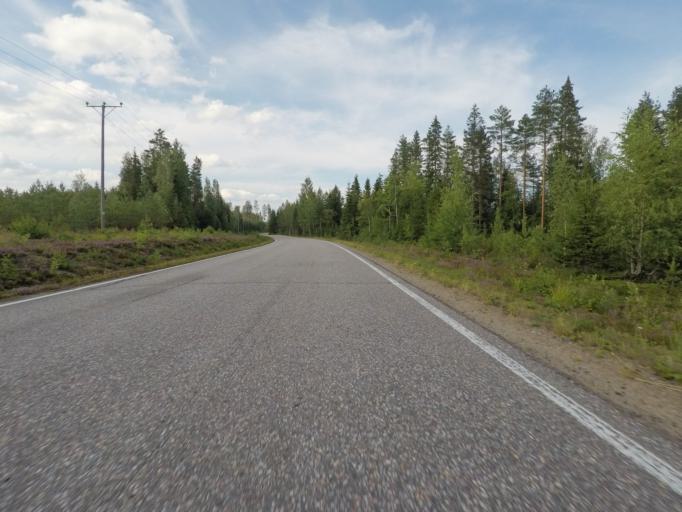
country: FI
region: Southern Savonia
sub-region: Savonlinna
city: Sulkava
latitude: 61.7436
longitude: 28.1994
